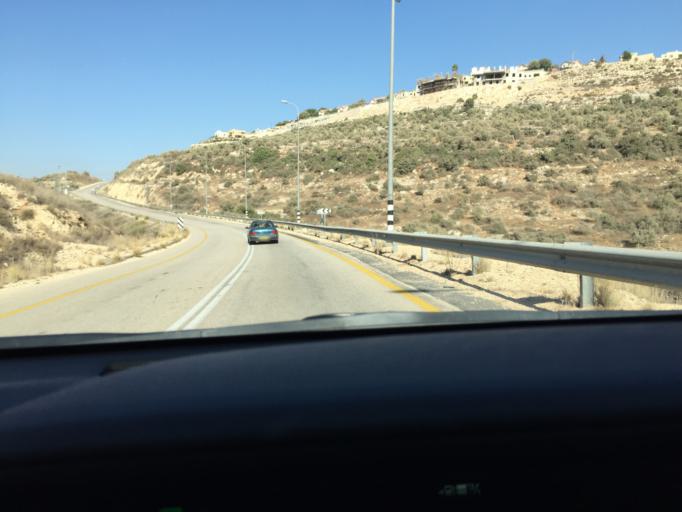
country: PS
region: West Bank
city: Rafat
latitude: 32.0647
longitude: 35.0487
